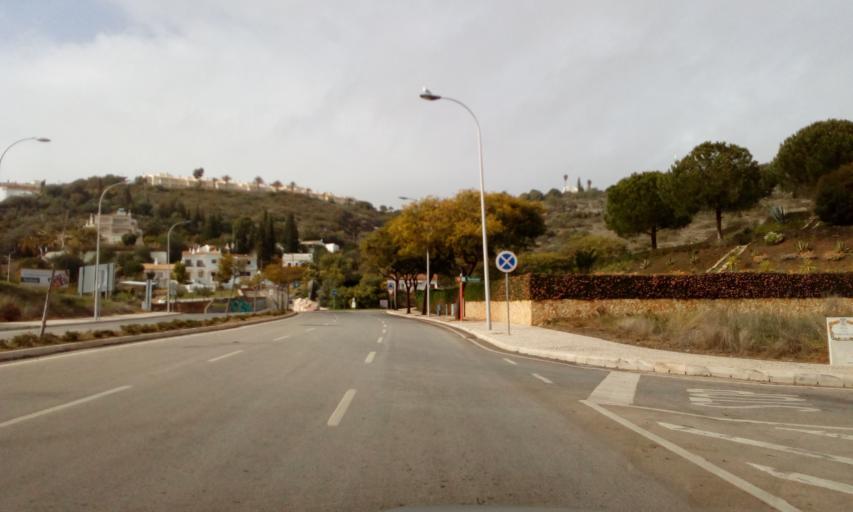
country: PT
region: Faro
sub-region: Albufeira
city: Albufeira
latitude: 37.0868
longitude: -8.2699
